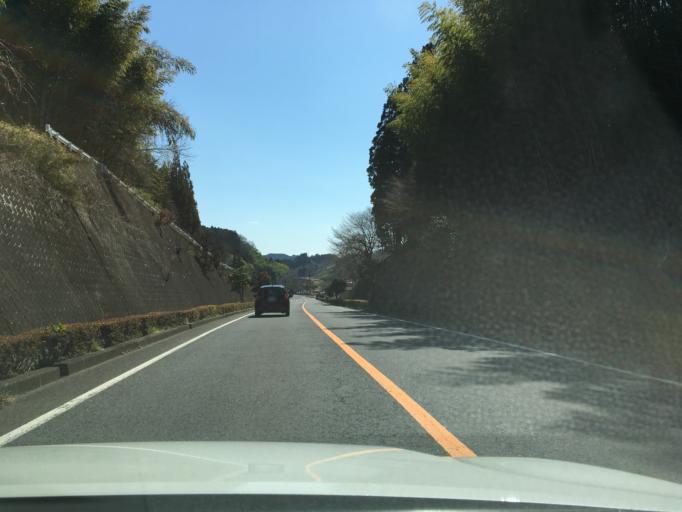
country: JP
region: Tochigi
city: Kuroiso
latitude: 37.0384
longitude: 140.1718
